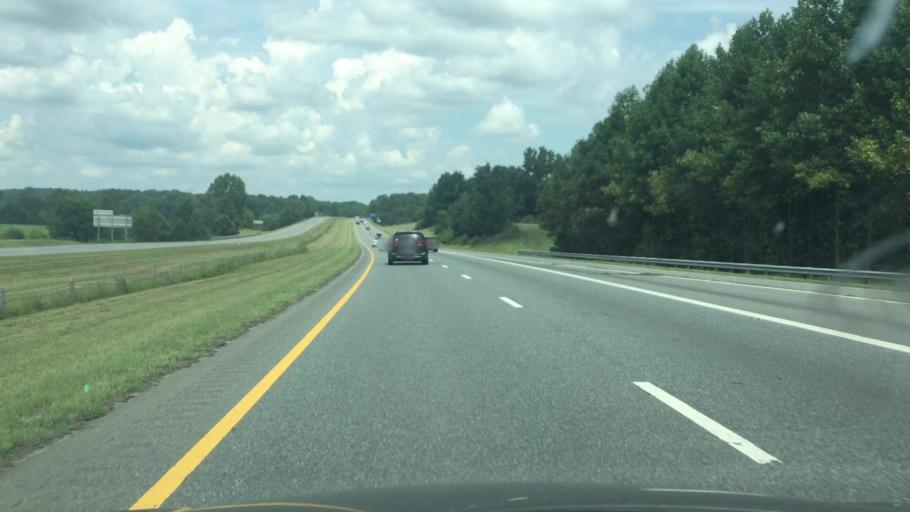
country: US
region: North Carolina
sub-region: Montgomery County
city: Biscoe
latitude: 35.4926
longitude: -79.7799
